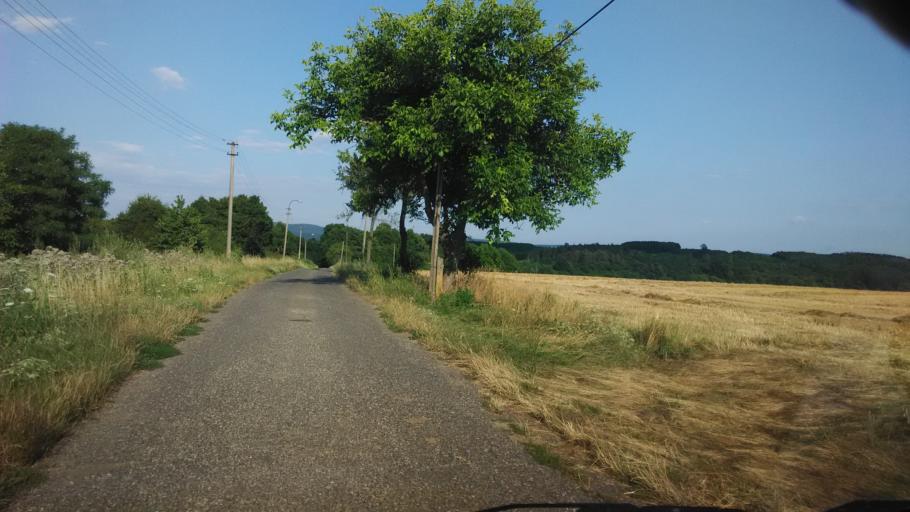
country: SK
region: Nitriansky
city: Levice
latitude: 48.2851
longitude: 18.6996
